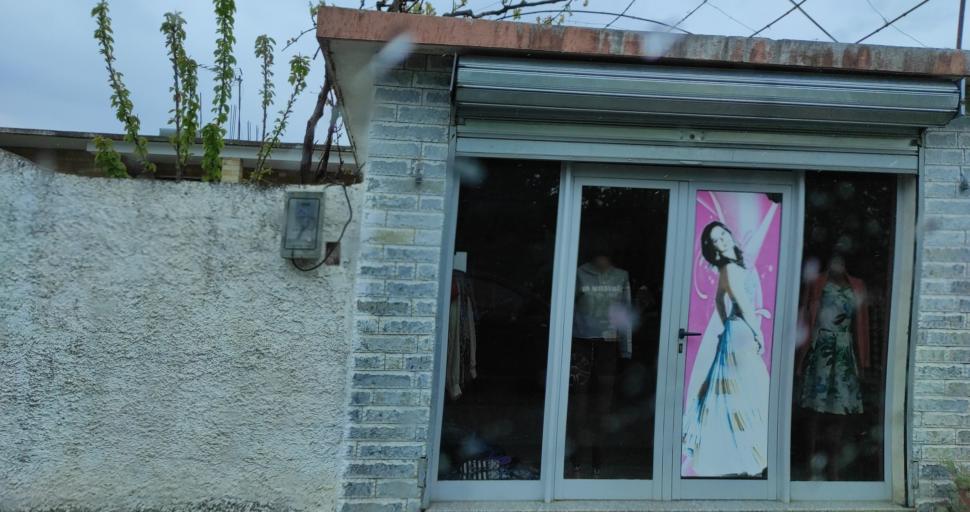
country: AL
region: Shkoder
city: Vukatane
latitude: 41.9990
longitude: 19.5505
